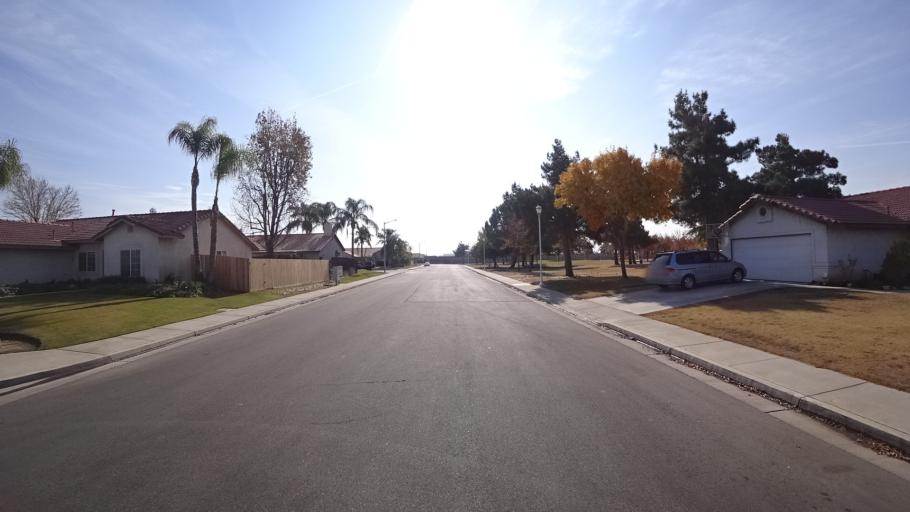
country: US
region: California
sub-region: Kern County
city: Greenacres
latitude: 35.3639
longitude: -119.1030
